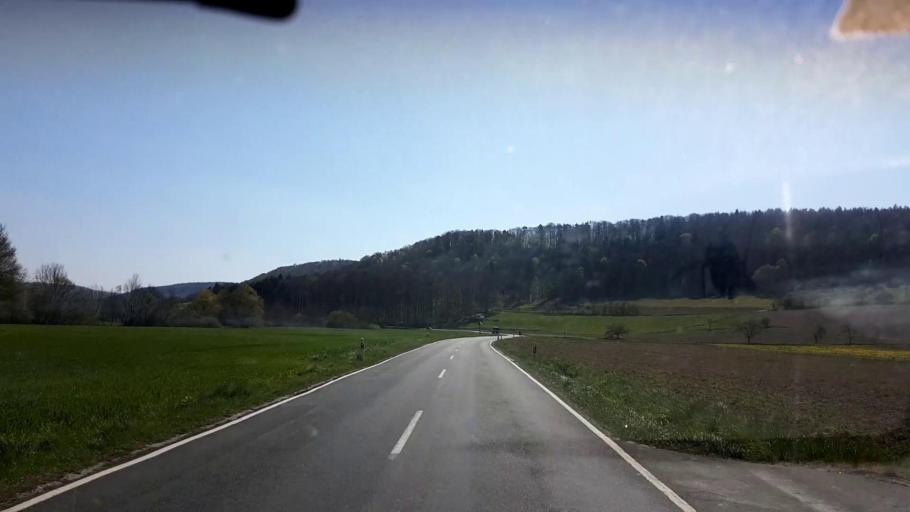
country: DE
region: Bavaria
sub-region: Upper Franconia
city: Unterleinleiter
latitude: 49.8328
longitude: 11.1895
